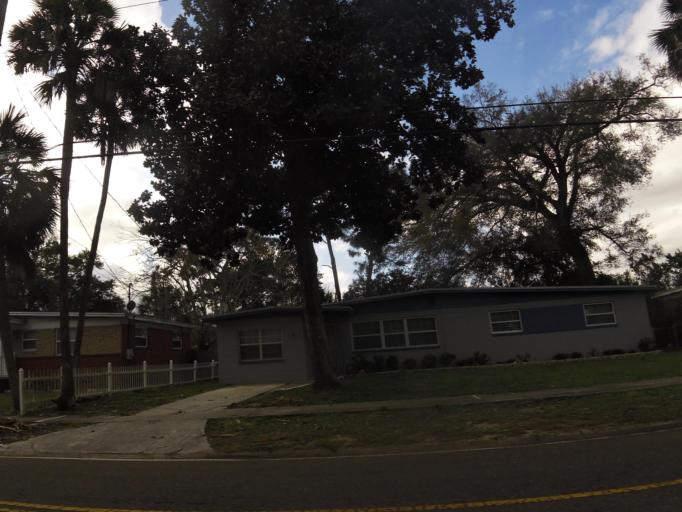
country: US
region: Florida
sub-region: Duval County
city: Jacksonville
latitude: 30.3634
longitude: -81.5889
